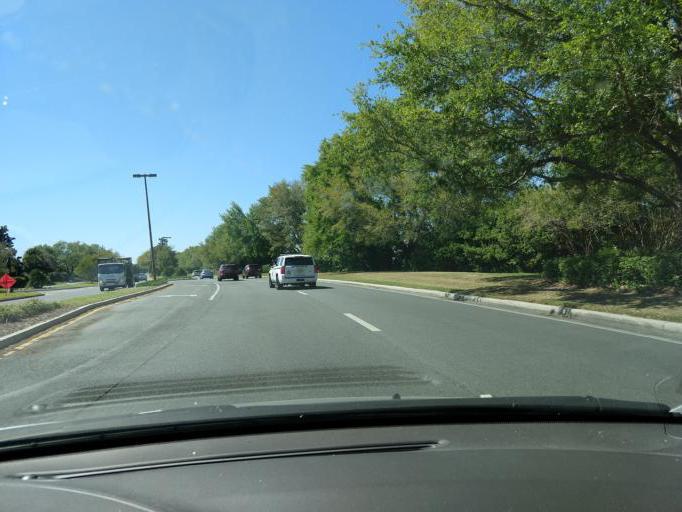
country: US
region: Florida
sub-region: Sumter County
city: The Villages
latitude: 28.9528
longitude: -81.9652
